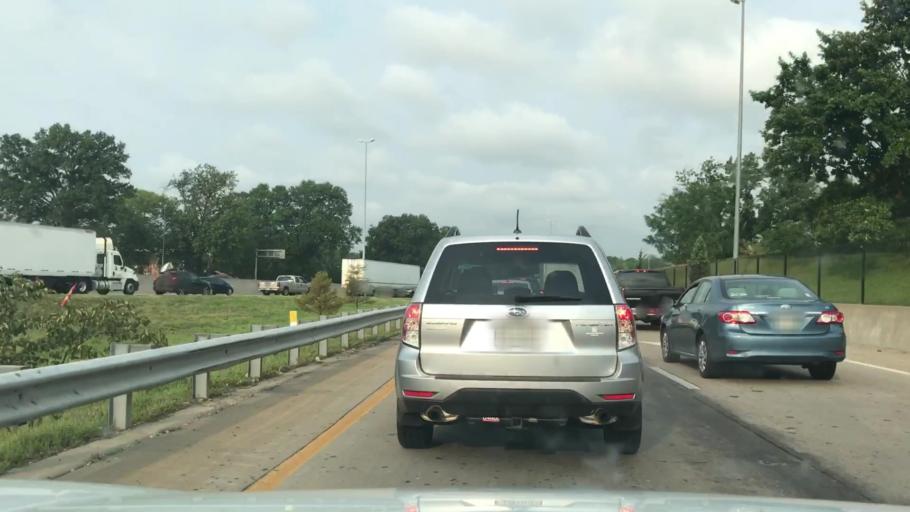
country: US
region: Missouri
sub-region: Saint Louis County
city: University City
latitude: 38.6325
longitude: -90.2881
